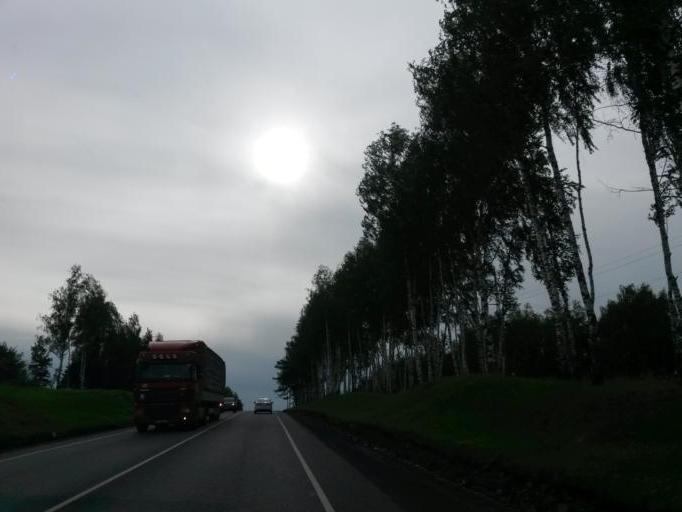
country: RU
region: Moskovskaya
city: Vostryakovo
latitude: 55.3340
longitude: 37.7575
